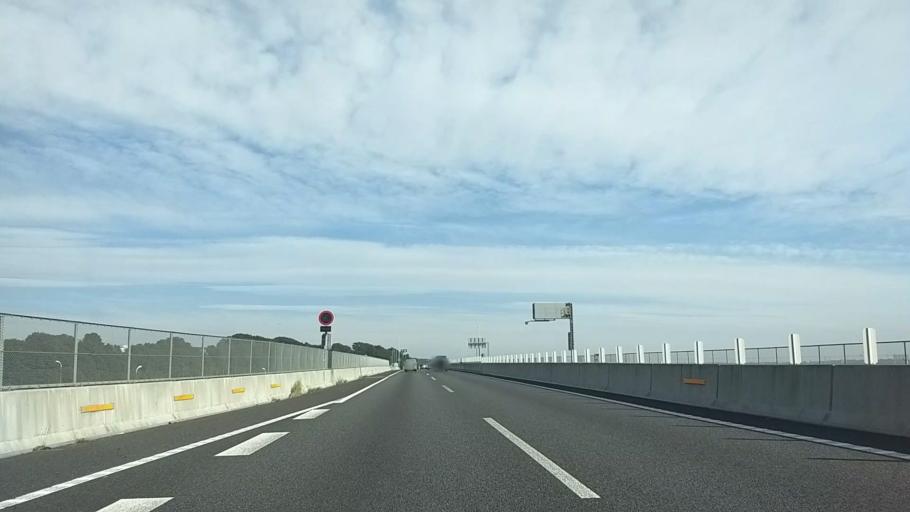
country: JP
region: Kanagawa
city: Zama
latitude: 35.4843
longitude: 139.3712
